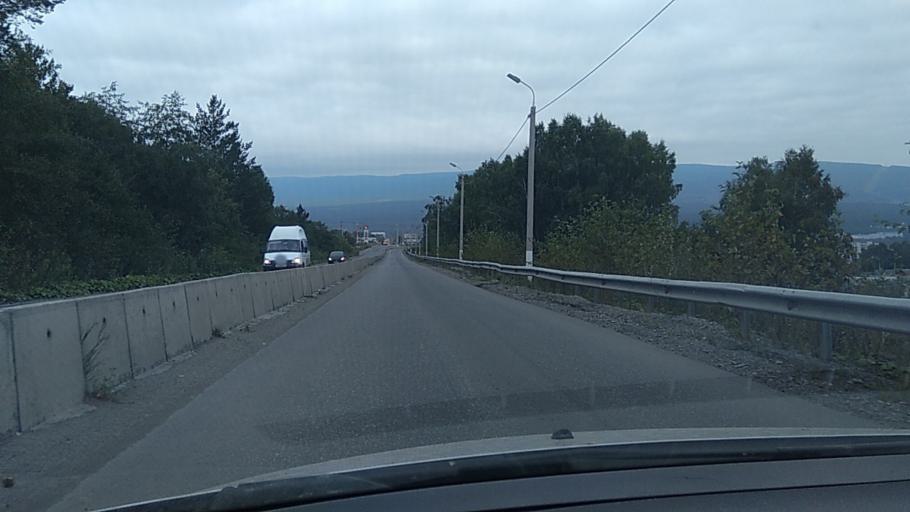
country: RU
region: Chelyabinsk
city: Zlatoust
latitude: 55.1172
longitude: 59.7411
